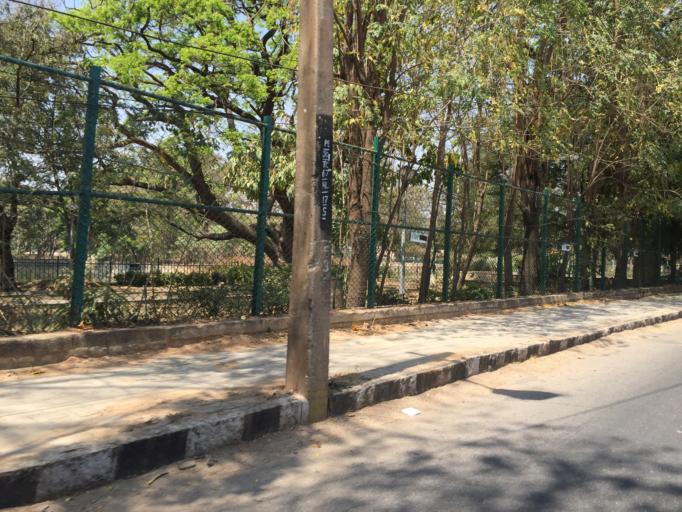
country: IN
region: Karnataka
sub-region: Bangalore Urban
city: Bangalore
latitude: 12.9863
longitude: 77.6225
